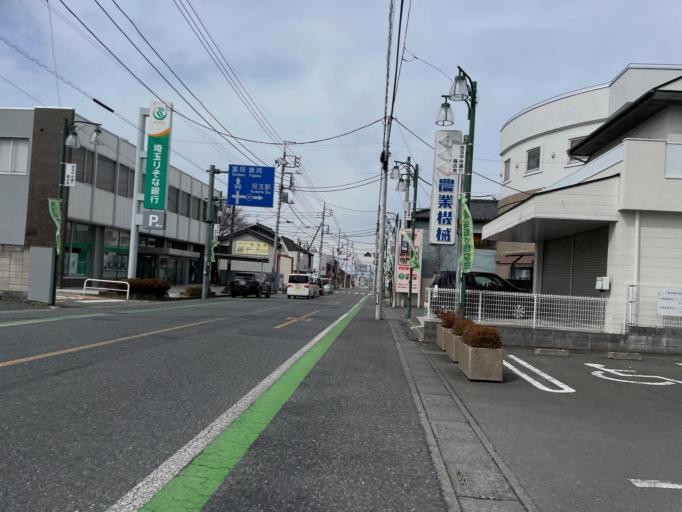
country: JP
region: Saitama
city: Kodamacho-kodamaminami
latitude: 36.1915
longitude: 139.1317
